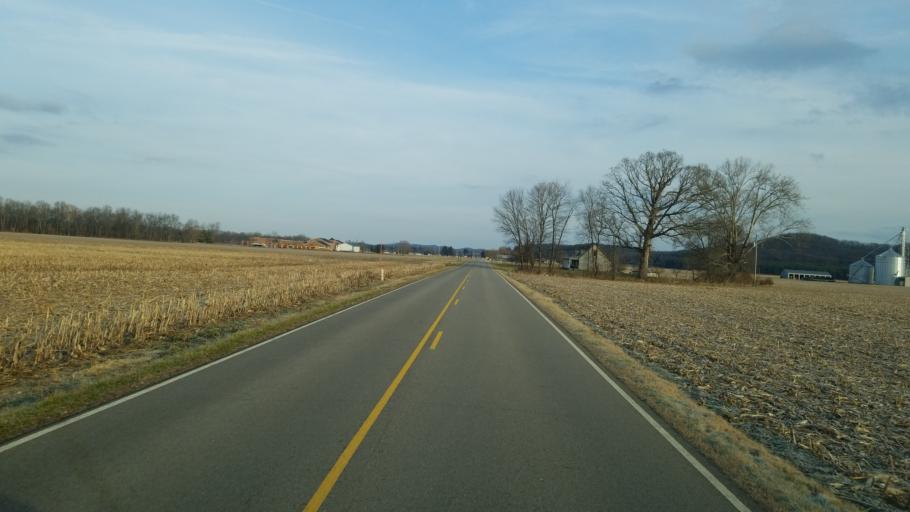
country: US
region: Ohio
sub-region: Ross County
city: Chillicothe
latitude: 39.2729
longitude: -82.8693
